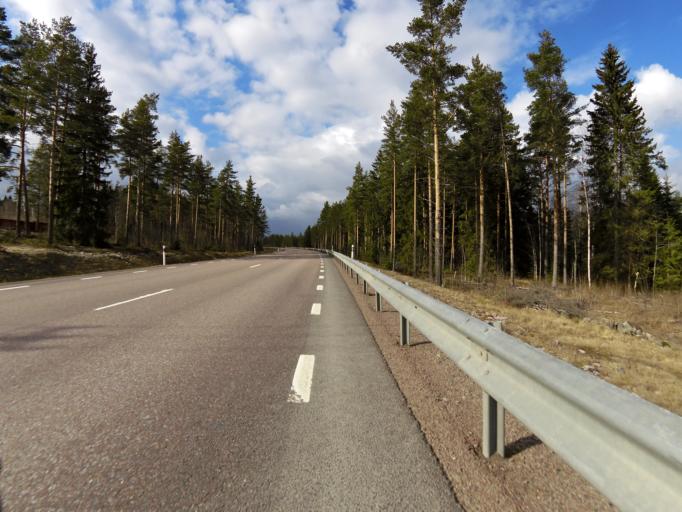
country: SE
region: Gaevleborg
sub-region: Hofors Kommun
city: Hofors
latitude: 60.4901
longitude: 16.4425
